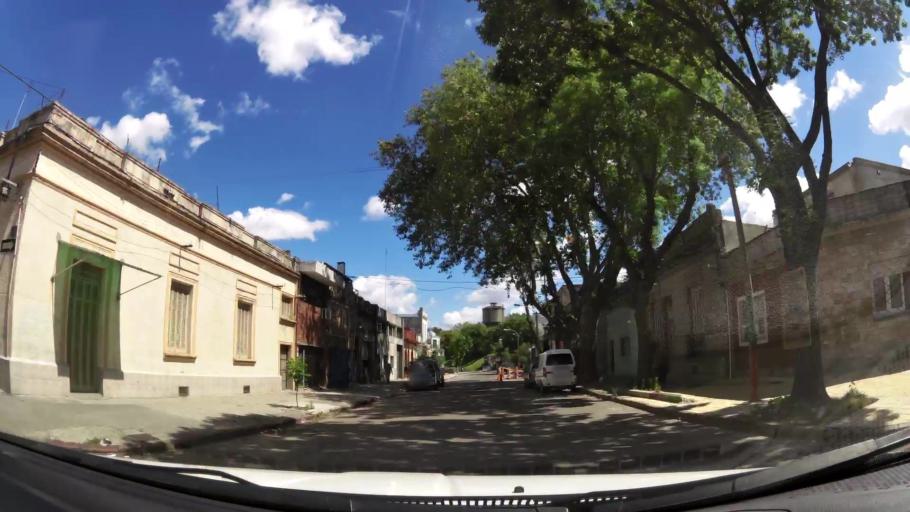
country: UY
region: Montevideo
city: Montevideo
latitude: -34.8816
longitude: -56.1889
